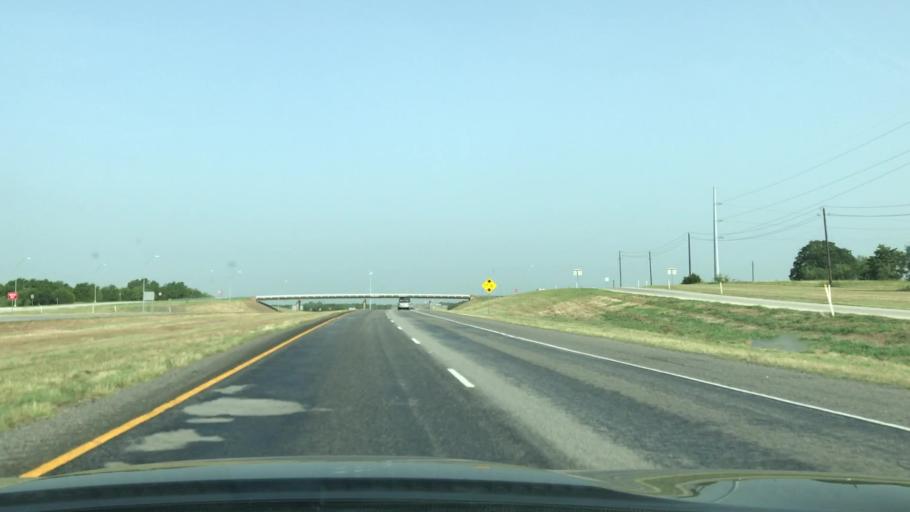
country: US
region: Texas
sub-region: Kaufman County
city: Terrell
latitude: 32.7284
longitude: -96.3368
